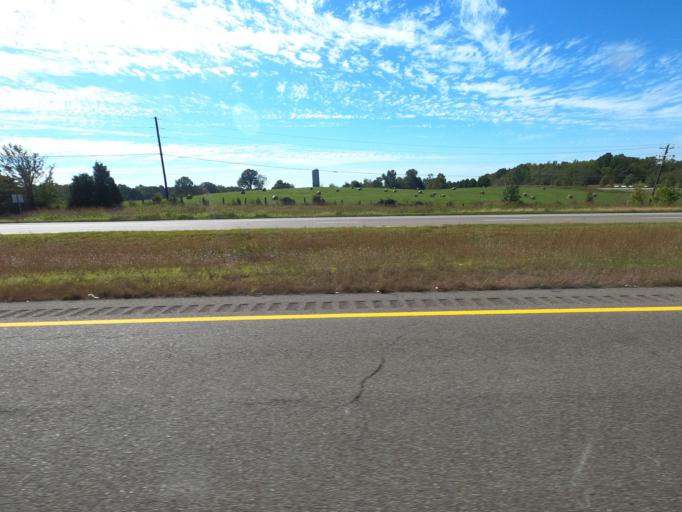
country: US
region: Tennessee
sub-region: Crockett County
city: Bells
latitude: 35.6789
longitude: -88.9714
